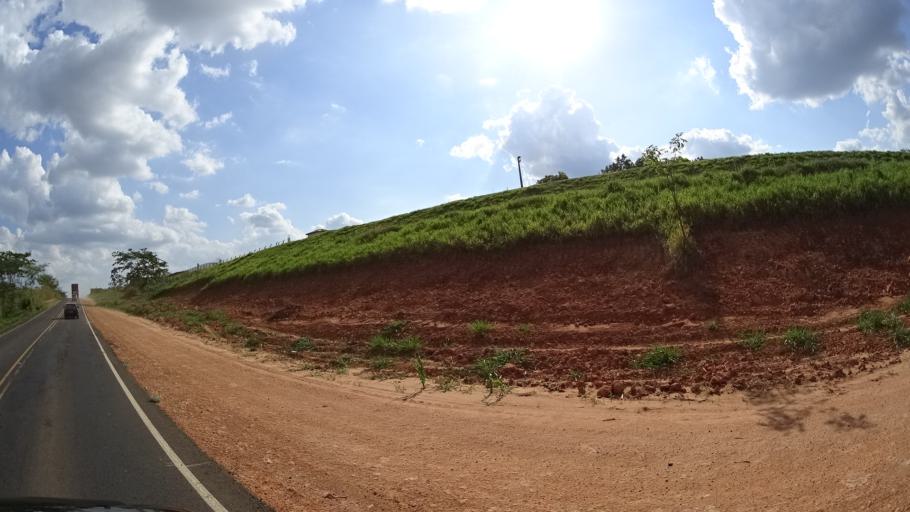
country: BR
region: Sao Paulo
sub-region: Urupes
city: Urupes
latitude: -21.1616
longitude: -49.2867
